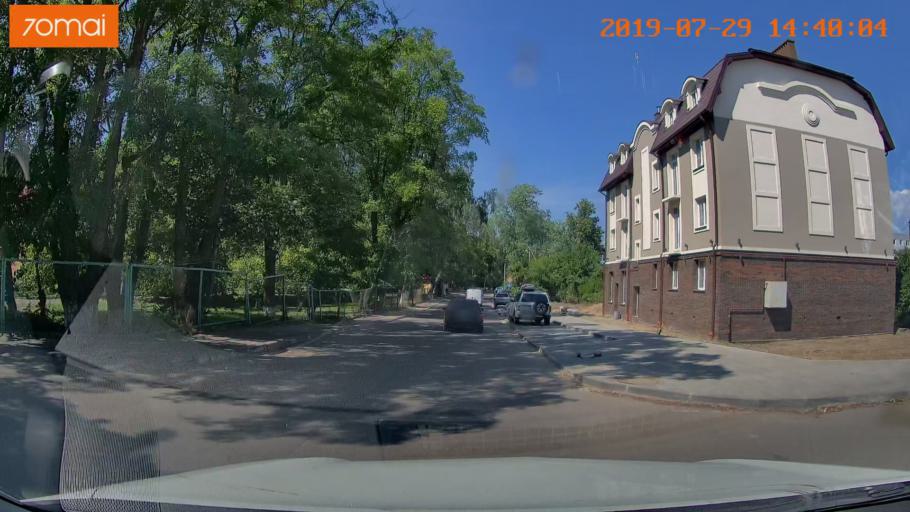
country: RU
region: Kaliningrad
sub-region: Gorod Kaliningrad
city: Baltiysk
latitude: 54.6534
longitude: 19.9024
